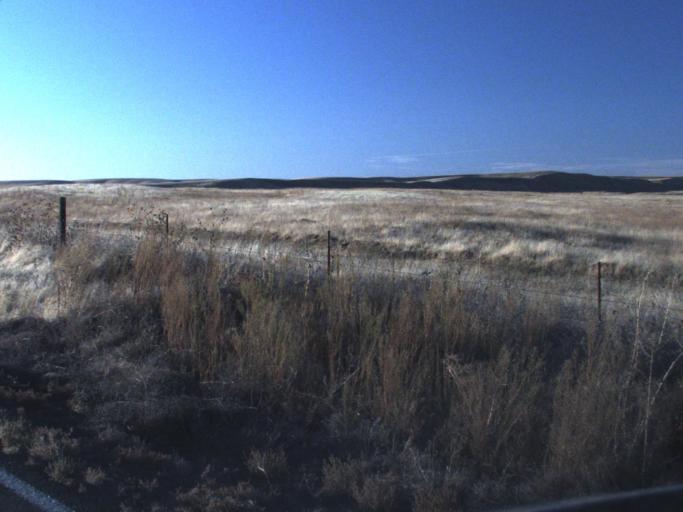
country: US
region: Washington
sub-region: Walla Walla County
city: Waitsburg
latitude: 46.6690
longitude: -118.2911
